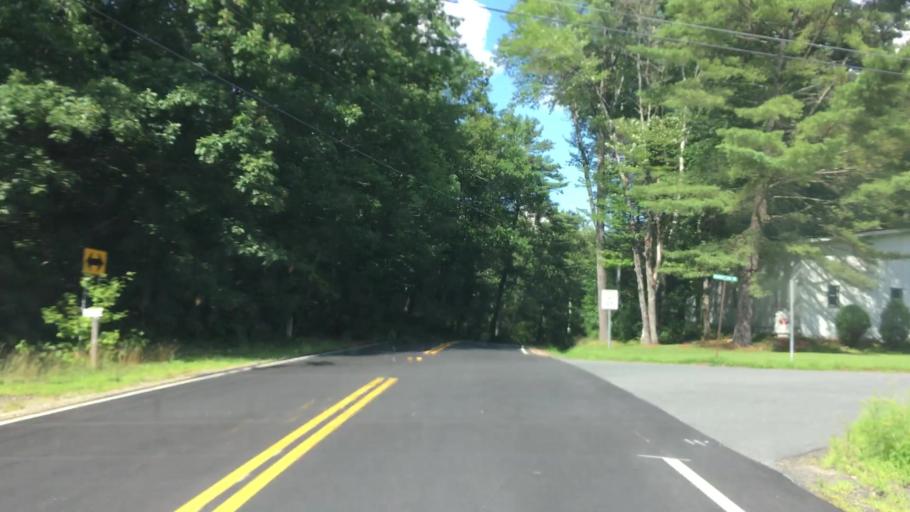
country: US
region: New Hampshire
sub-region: Grafton County
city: North Haverhill
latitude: 44.1206
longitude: -71.9351
